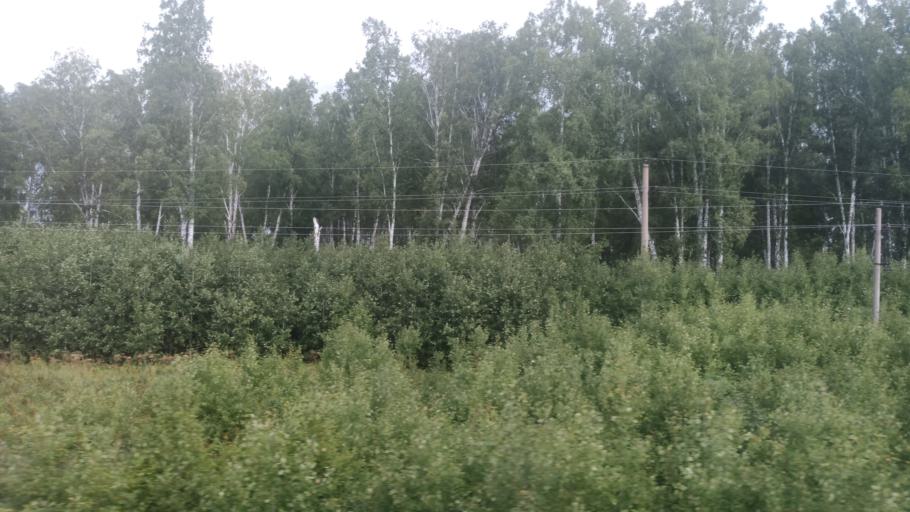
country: RU
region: Altai Krai
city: Nalobikha
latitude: 53.2311
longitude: 84.5057
